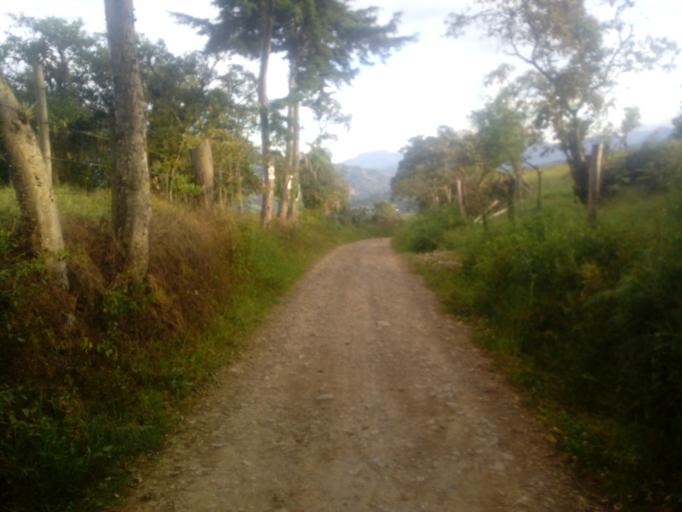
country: CO
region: Cundinamarca
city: Tenza
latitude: 5.0899
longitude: -73.4137
